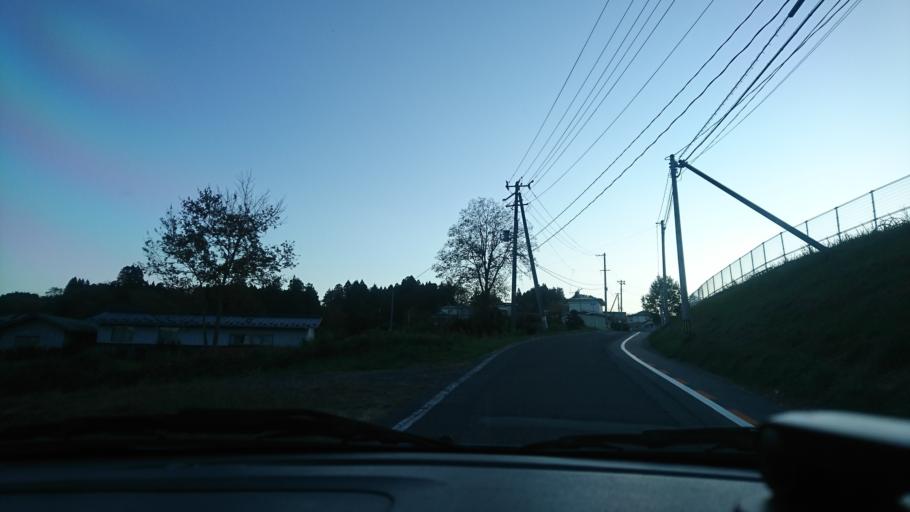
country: JP
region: Iwate
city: Ichinoseki
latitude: 38.8661
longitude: 141.3530
